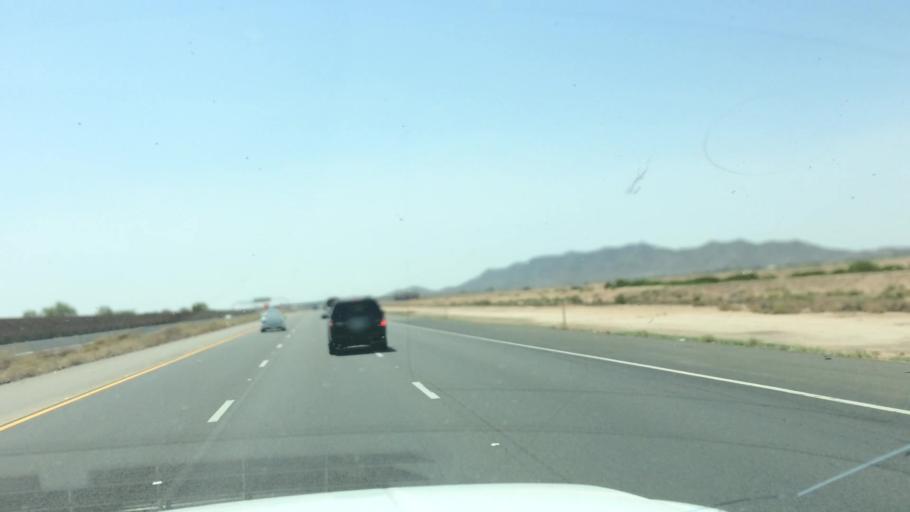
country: US
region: Arizona
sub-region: Pinal County
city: Casa Grande
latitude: 32.8738
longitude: -111.6881
